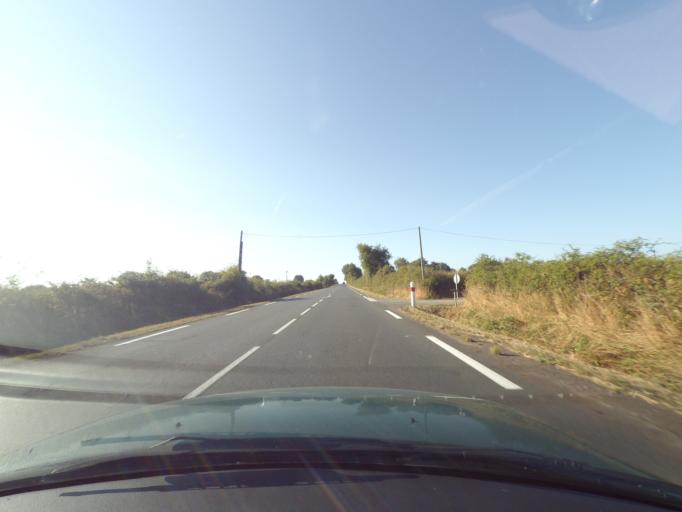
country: FR
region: Poitou-Charentes
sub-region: Departement des Deux-Sevres
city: Viennay
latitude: 46.7370
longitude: -0.3017
